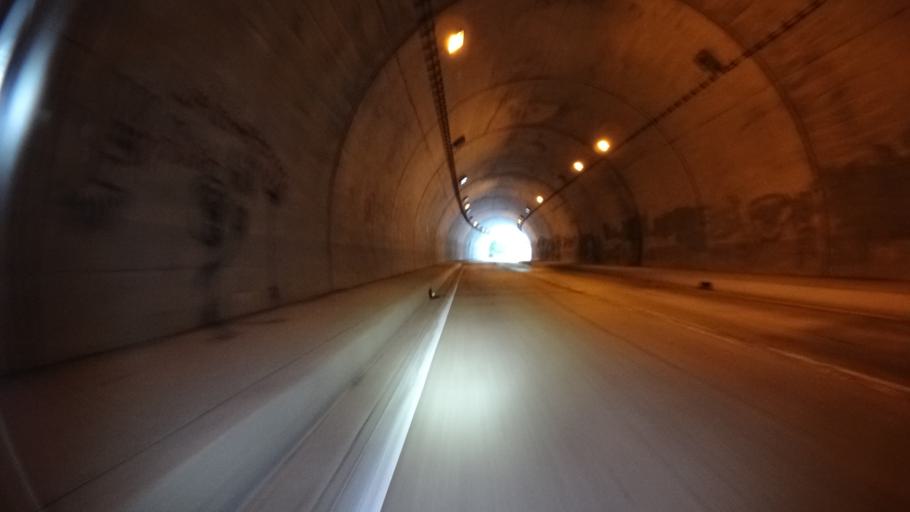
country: JP
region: Kanagawa
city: Hadano
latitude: 35.5115
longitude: 139.2313
